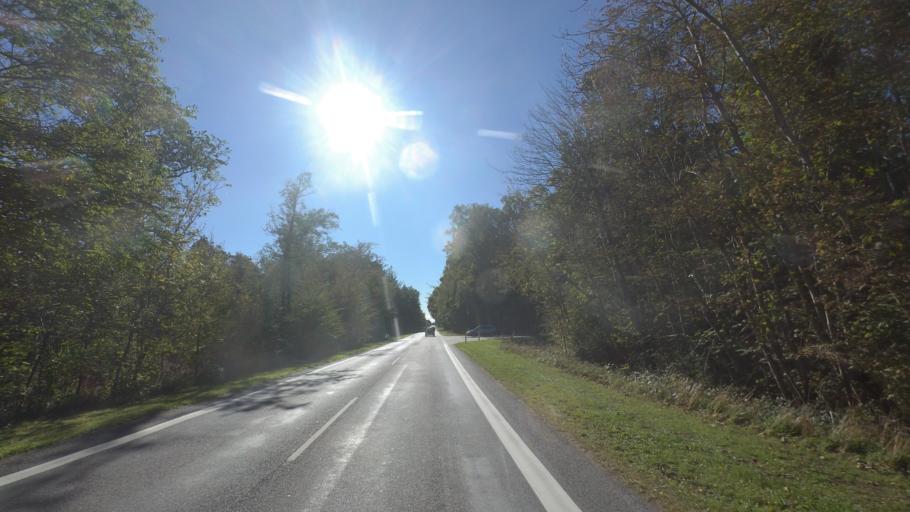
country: DK
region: Capital Region
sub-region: Bornholm Kommune
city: Nexo
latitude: 55.0514
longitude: 15.1206
